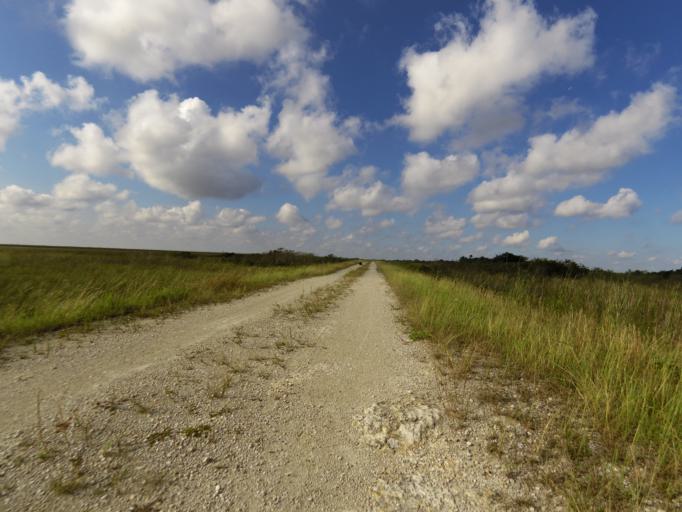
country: US
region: Florida
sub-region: Broward County
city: Weston
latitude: 26.0523
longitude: -80.4682
